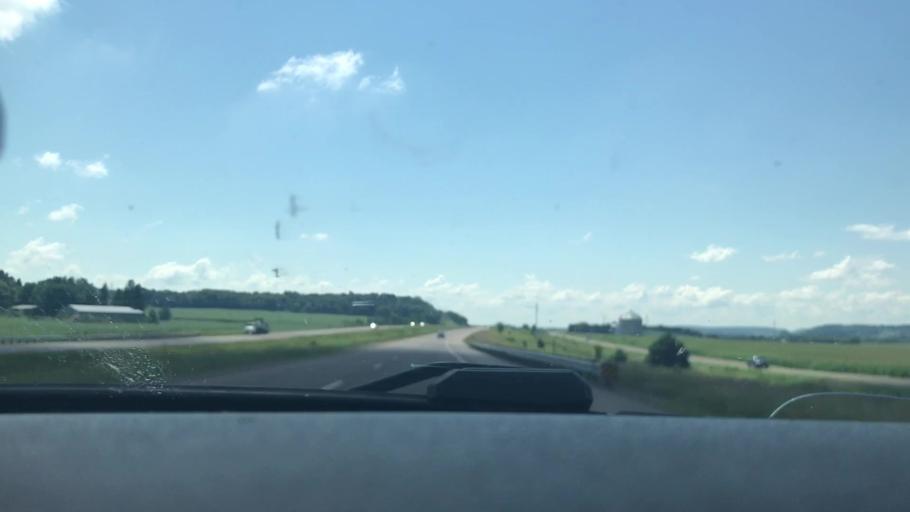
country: US
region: Wisconsin
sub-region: Chippewa County
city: Bloomer
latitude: 45.0364
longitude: -91.4551
